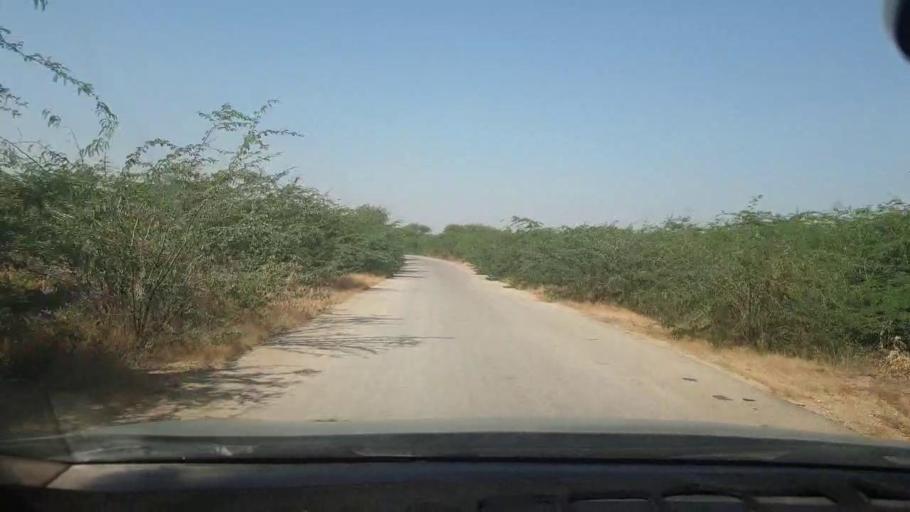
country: PK
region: Sindh
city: Malir Cantonment
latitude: 25.1616
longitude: 67.1609
